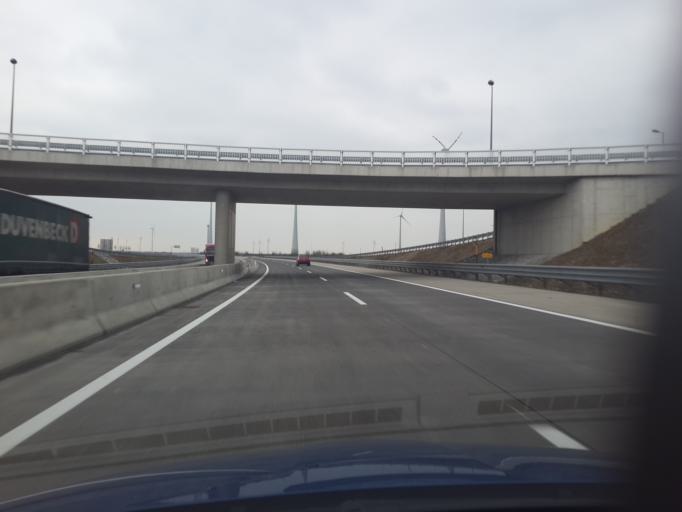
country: AT
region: Lower Austria
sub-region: Politischer Bezirk Bruck an der Leitha
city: Berg
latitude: 48.0818
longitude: 17.0314
